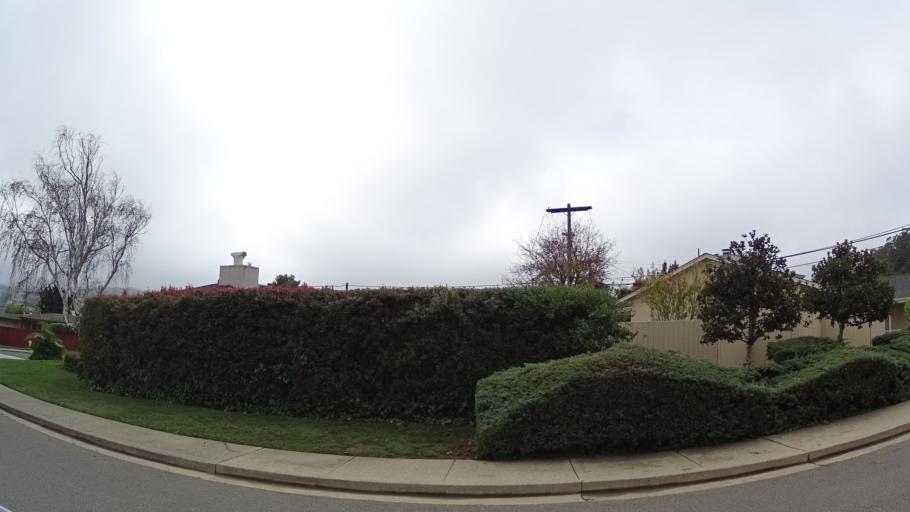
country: US
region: California
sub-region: San Mateo County
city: San Bruno
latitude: 37.6076
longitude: -122.4186
